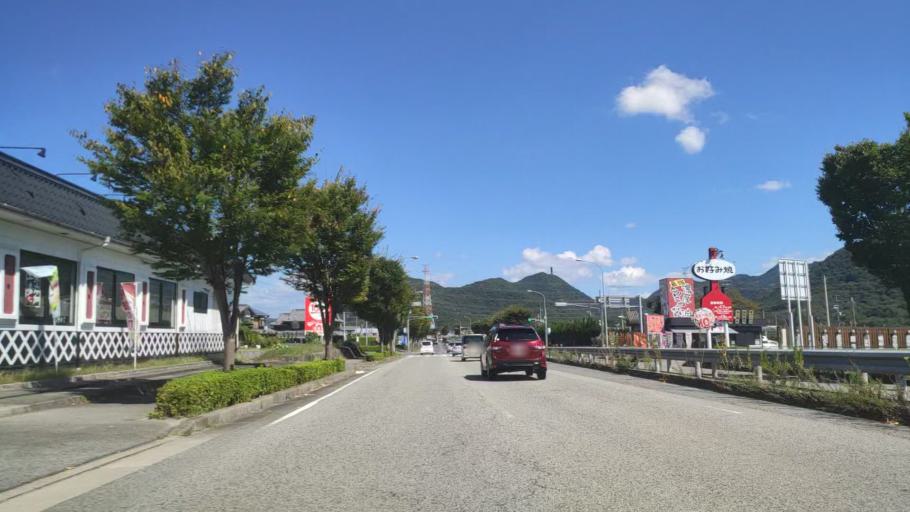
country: JP
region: Hyogo
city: Nishiwaki
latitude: 34.9516
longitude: 134.9713
